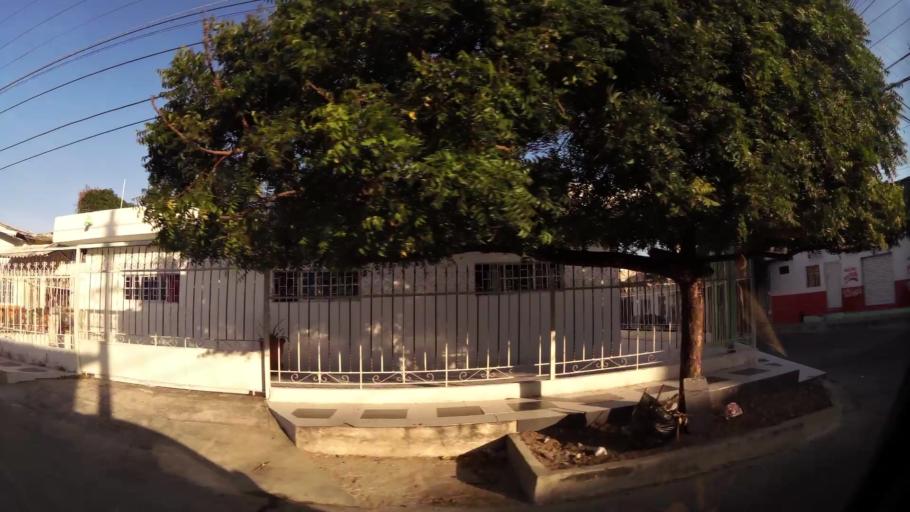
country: CO
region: Atlantico
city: Barranquilla
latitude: 10.9773
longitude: -74.7922
